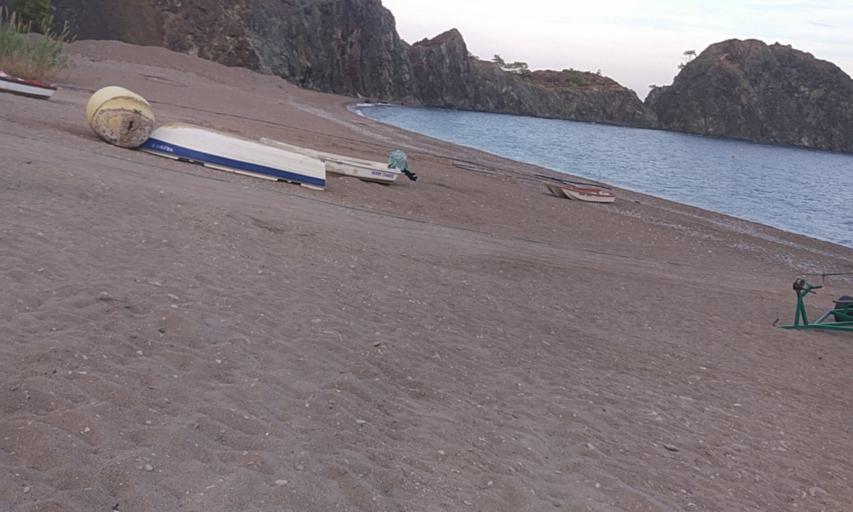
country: TR
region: Antalya
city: Tekirova
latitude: 36.4211
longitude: 30.4863
